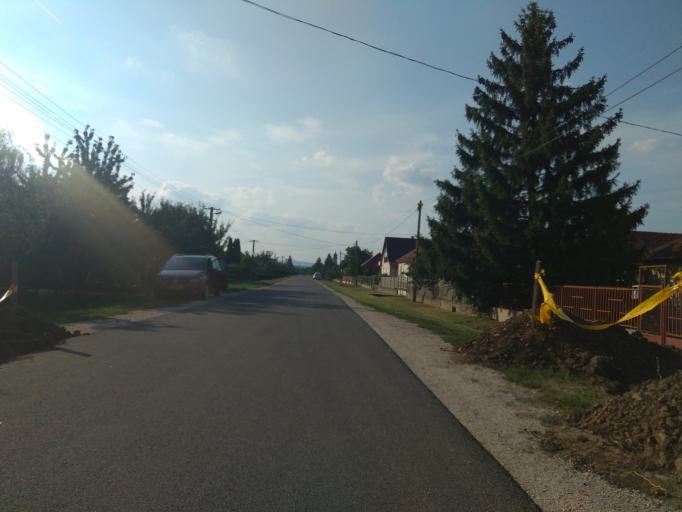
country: HU
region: Borsod-Abauj-Zemplen
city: Emod
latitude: 47.8861
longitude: 20.7692
